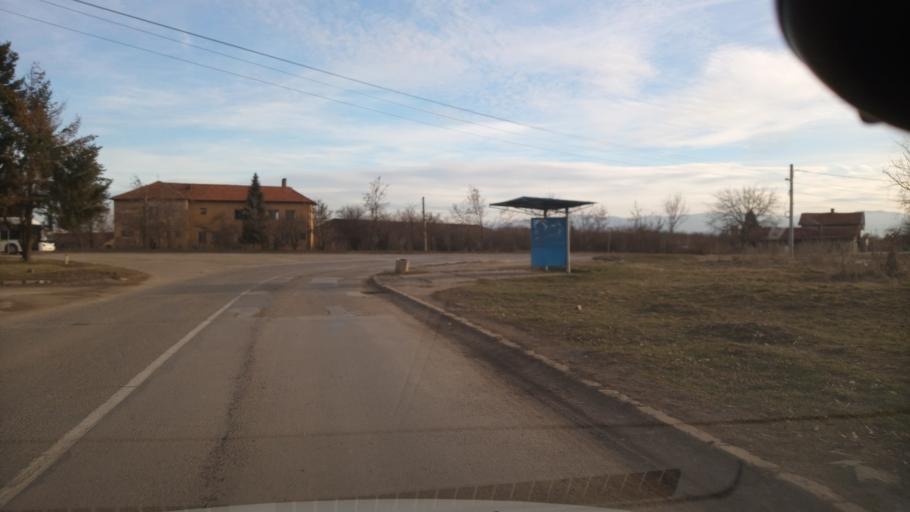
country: BG
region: Sofia-Capital
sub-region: Stolichna Obshtina
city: Bukhovo
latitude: 42.7272
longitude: 23.5552
